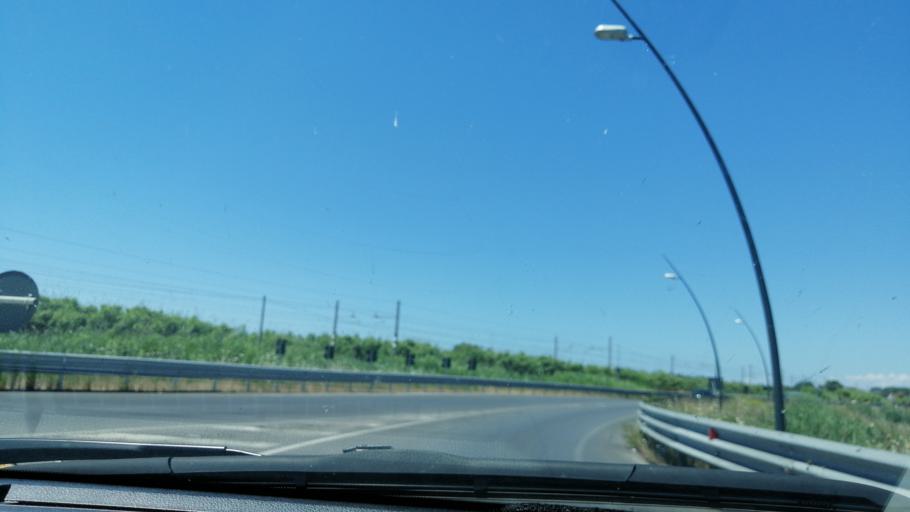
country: IT
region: Tuscany
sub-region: Province of Pisa
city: Migliarino
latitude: 43.7781
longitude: 10.3309
